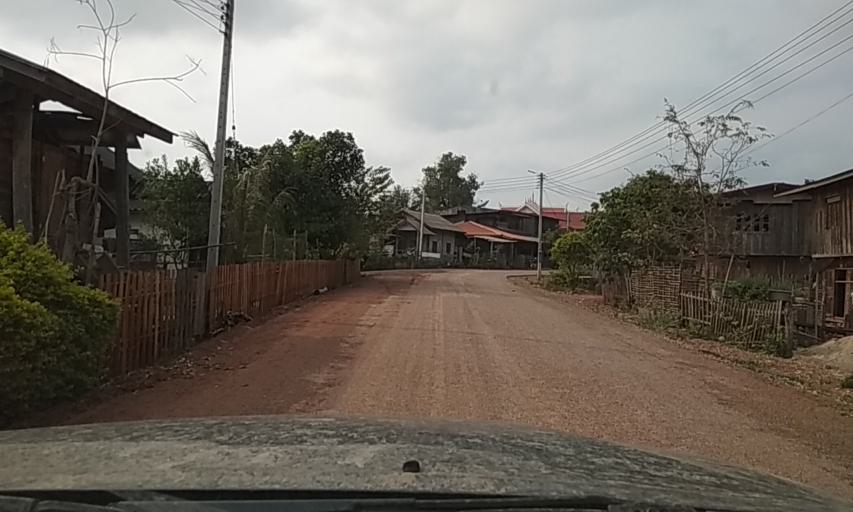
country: TH
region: Nan
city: Mae Charim
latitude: 18.4058
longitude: 101.1736
